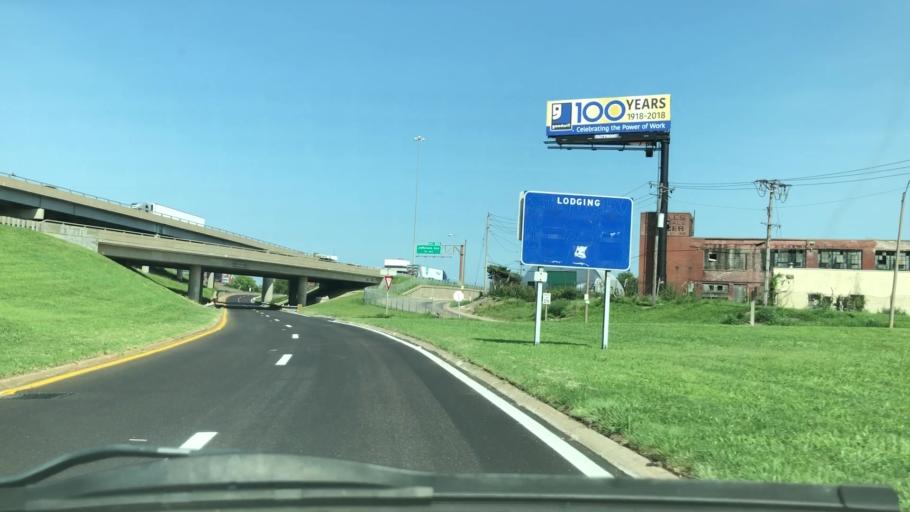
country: US
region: Missouri
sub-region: City of Saint Louis
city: St. Louis
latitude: 38.6305
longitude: -90.2329
